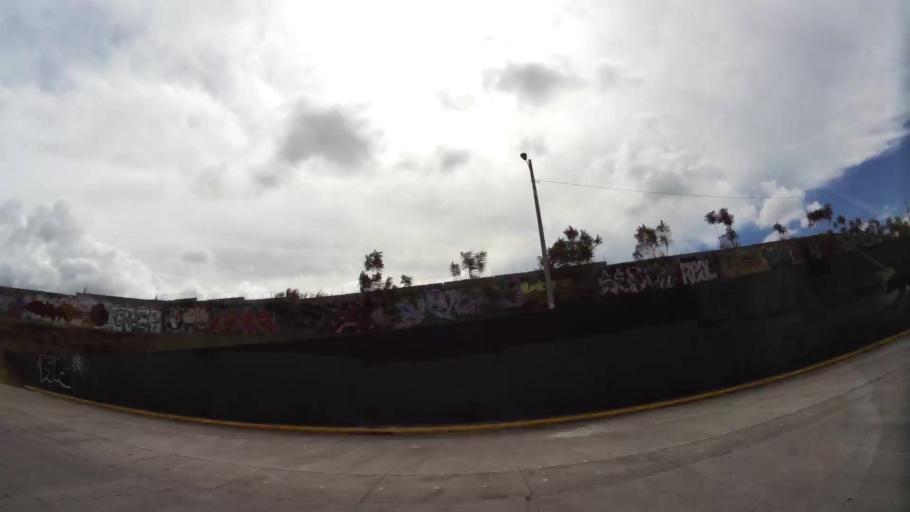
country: GT
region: Guatemala
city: Santa Catarina Pinula
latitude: 14.5970
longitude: -90.5247
